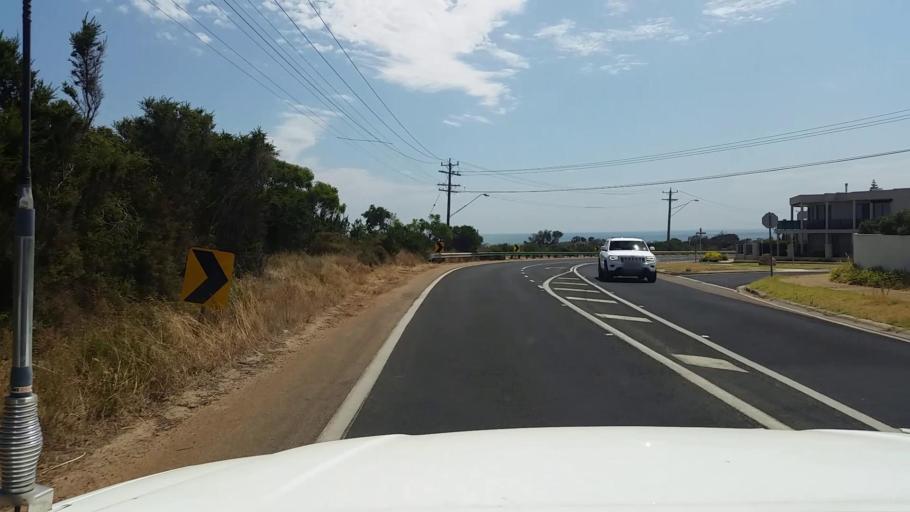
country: AU
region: Victoria
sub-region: Mornington Peninsula
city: Mornington
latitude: -38.2302
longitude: 145.0263
